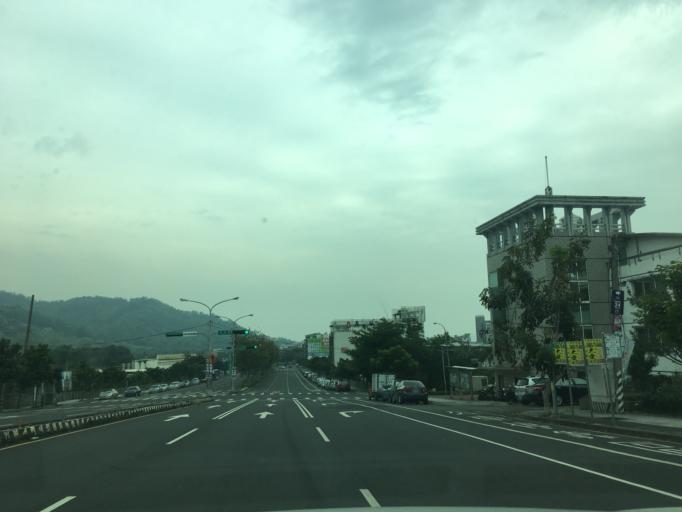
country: TW
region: Taiwan
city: Zhongxing New Village
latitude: 23.9796
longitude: 120.6895
